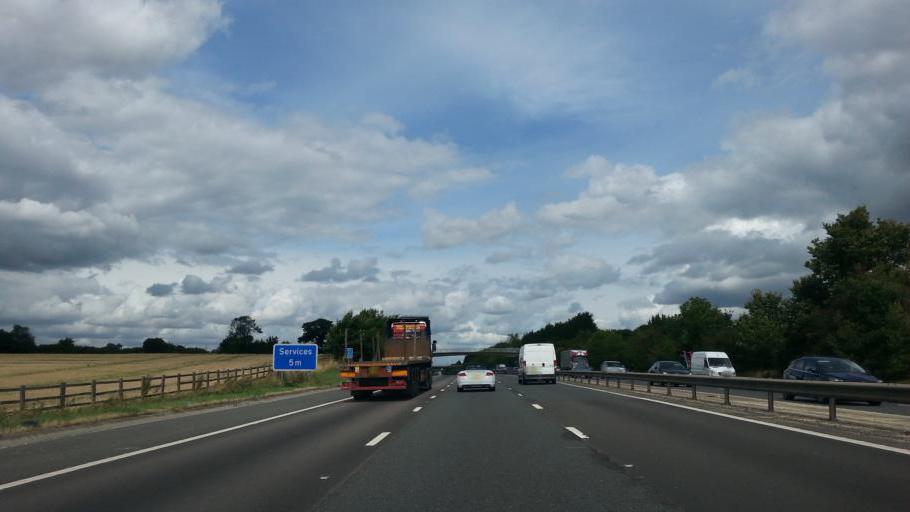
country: GB
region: England
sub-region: Hertfordshire
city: Sawbridgeworth
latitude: 51.7977
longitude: 0.1748
